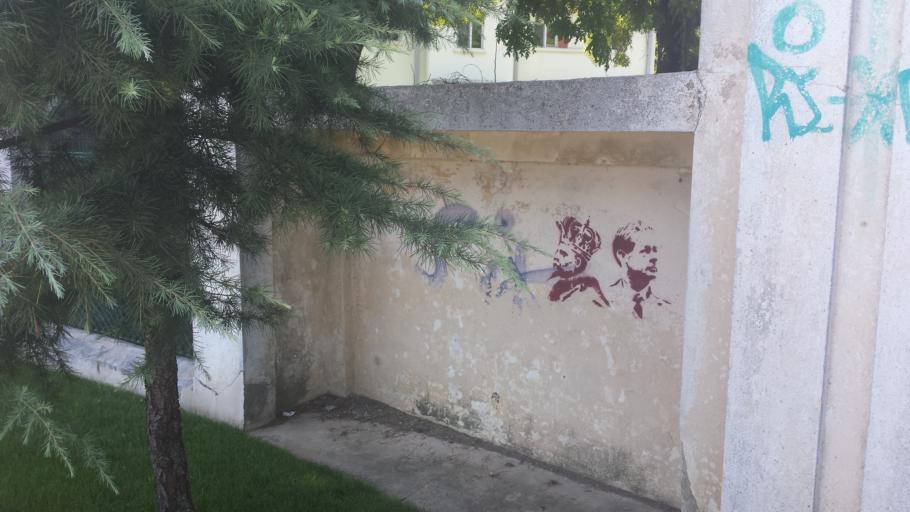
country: RO
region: Giurgiu
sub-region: Comuna Daia
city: Plopsoru
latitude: 44.0000
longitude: 26.0000
